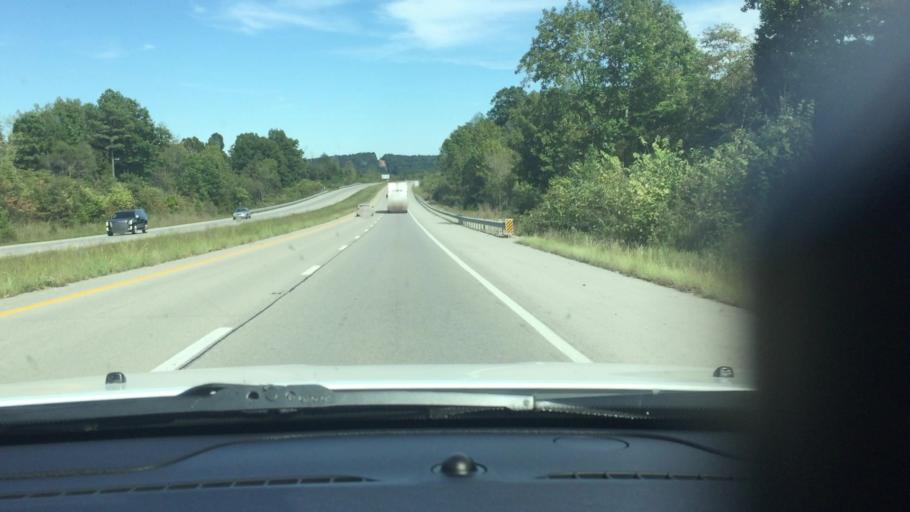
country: US
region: Kentucky
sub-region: Caldwell County
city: Princeton
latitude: 37.1360
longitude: -87.8613
